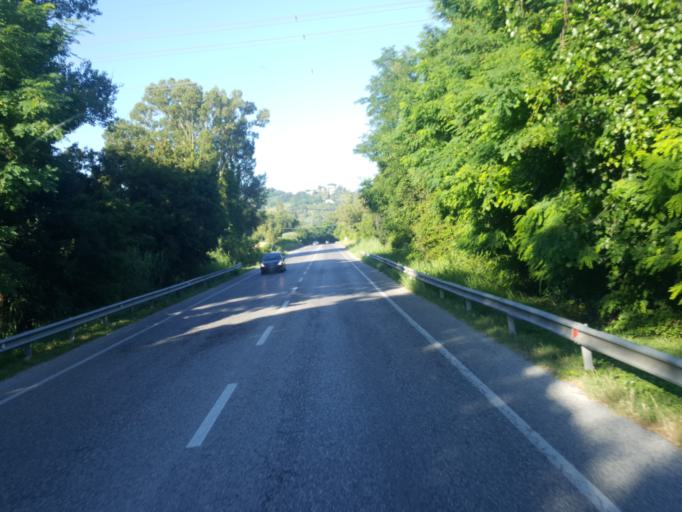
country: IT
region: The Marches
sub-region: Provincia di Pesaro e Urbino
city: Borgo Santa Maria
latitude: 43.8574
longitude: 12.8106
